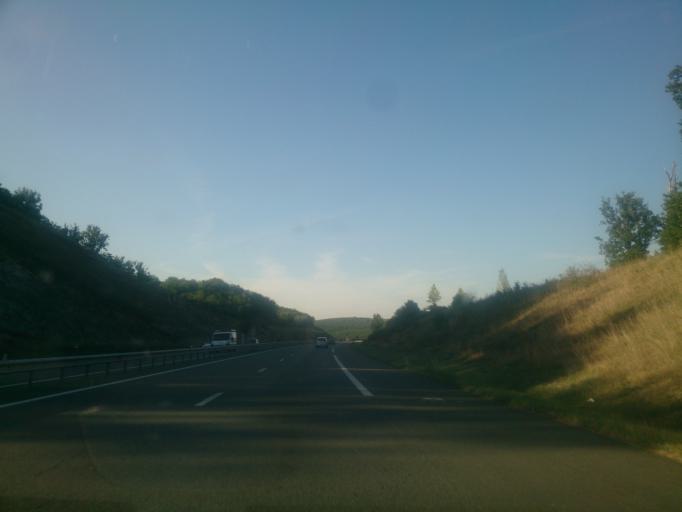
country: FR
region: Midi-Pyrenees
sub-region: Departement du Lot
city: Le Vigan
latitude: 44.7578
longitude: 1.5395
